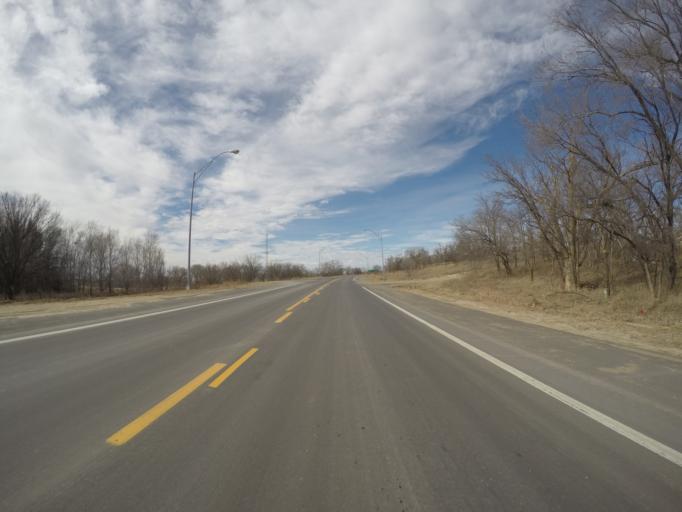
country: US
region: Nebraska
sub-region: Franklin County
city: Franklin
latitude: 40.0898
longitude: -98.7631
